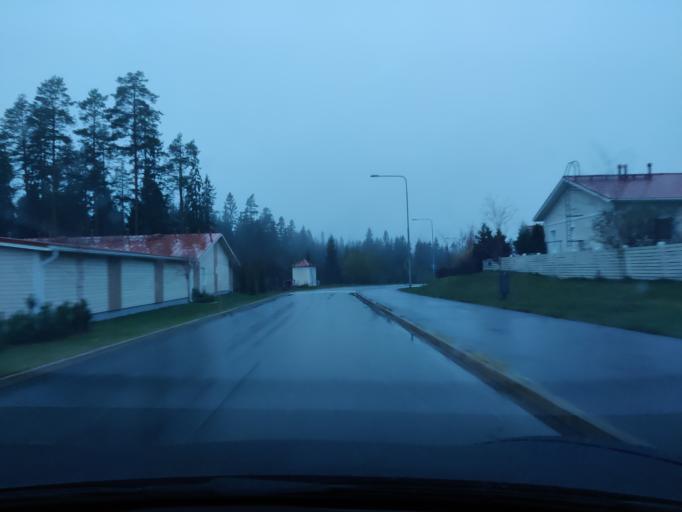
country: FI
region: Northern Savo
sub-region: Kuopio
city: Kuopio
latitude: 62.8285
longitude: 27.7184
